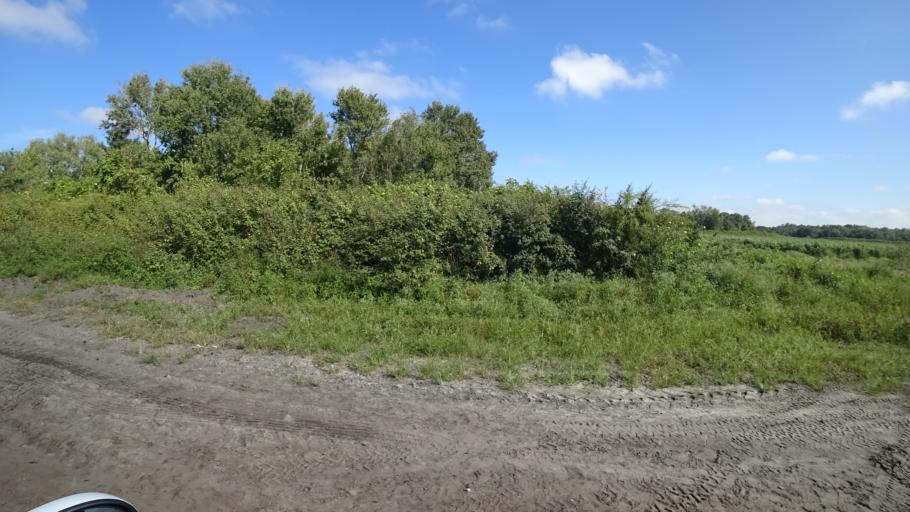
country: US
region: Florida
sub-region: DeSoto County
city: Arcadia
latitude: 27.2853
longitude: -82.0786
